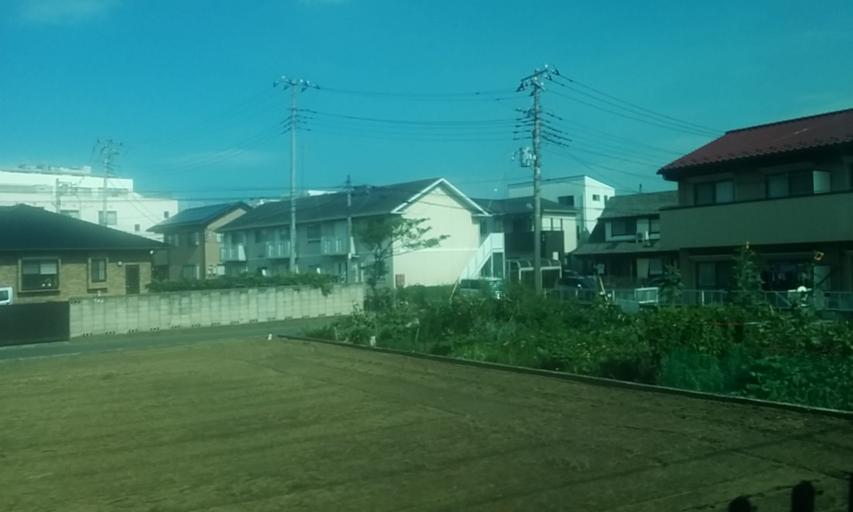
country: JP
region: Saitama
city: Shiraoka
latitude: 36.0133
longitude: 139.6664
